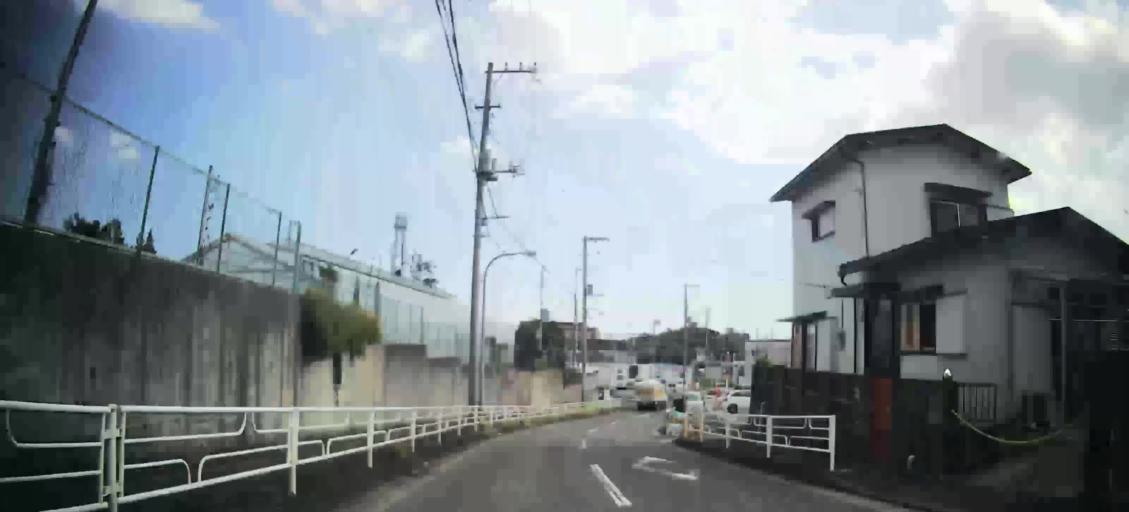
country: JP
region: Kanagawa
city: Yokohama
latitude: 35.4817
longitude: 139.5765
